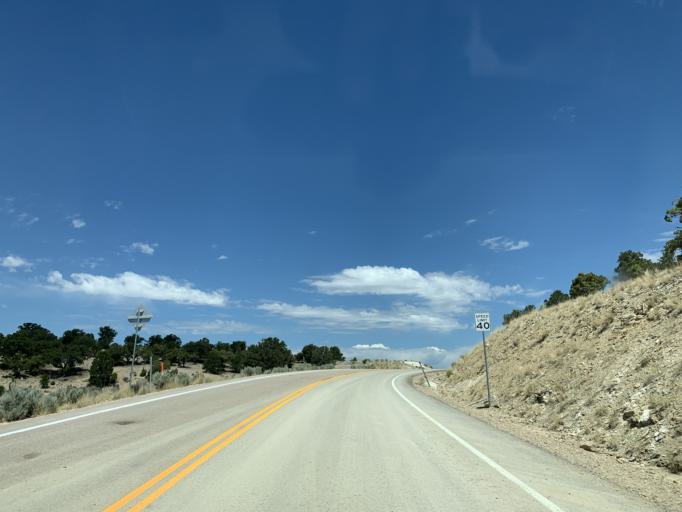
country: US
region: Utah
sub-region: Duchesne County
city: Duchesne
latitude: 39.8816
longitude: -110.2320
